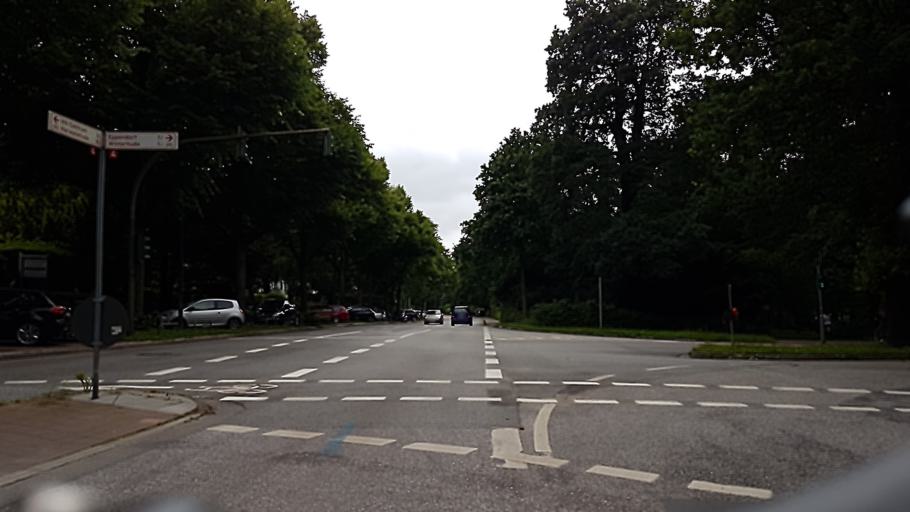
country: DE
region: Hamburg
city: Hamburg-Nord
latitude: 53.5784
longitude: 9.9975
